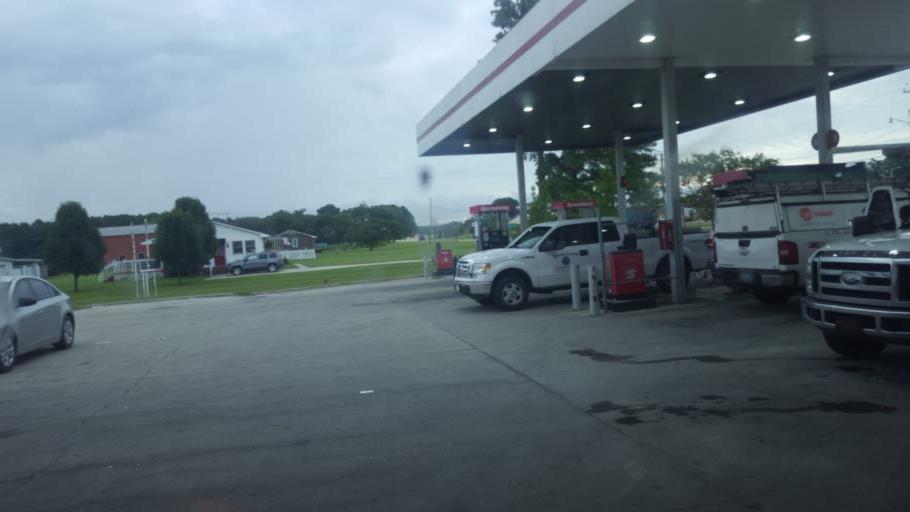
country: US
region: North Carolina
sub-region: Tyrrell County
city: Columbia
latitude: 35.9192
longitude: -76.2370
